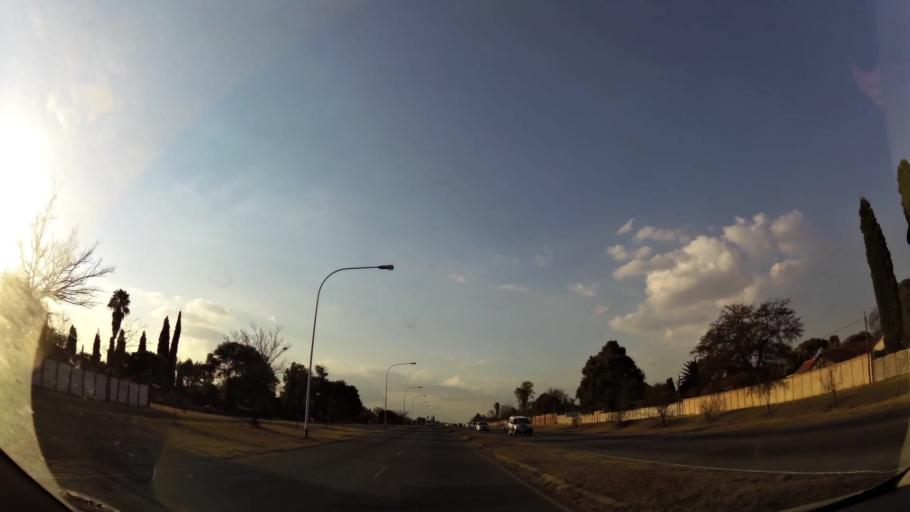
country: ZA
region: Gauteng
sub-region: Ekurhuleni Metropolitan Municipality
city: Boksburg
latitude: -26.2661
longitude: 28.2413
